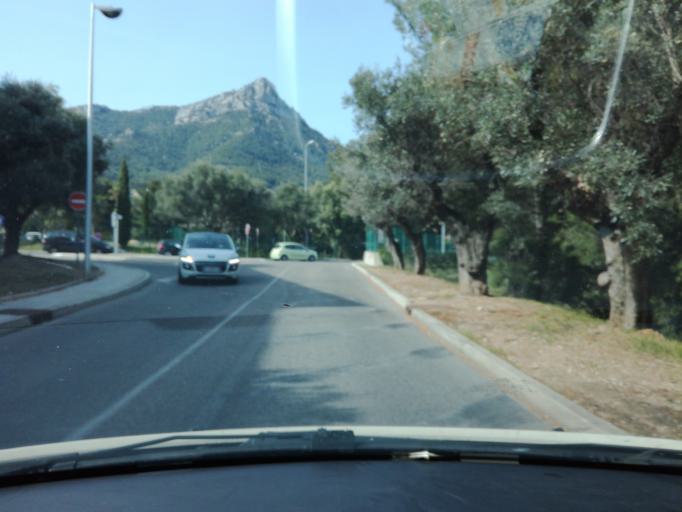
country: FR
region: Provence-Alpes-Cote d'Azur
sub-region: Departement du Var
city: La Garde
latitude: 43.1423
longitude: 6.0125
